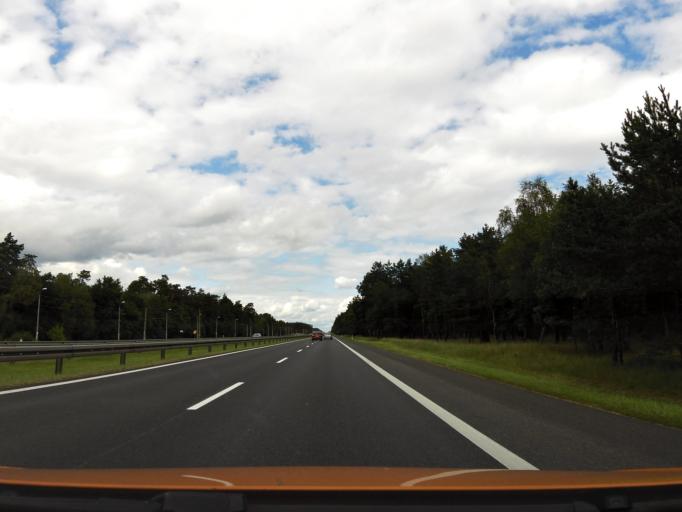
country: PL
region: West Pomeranian Voivodeship
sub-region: Powiat goleniowski
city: Goleniow
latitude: 53.4931
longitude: 14.7963
